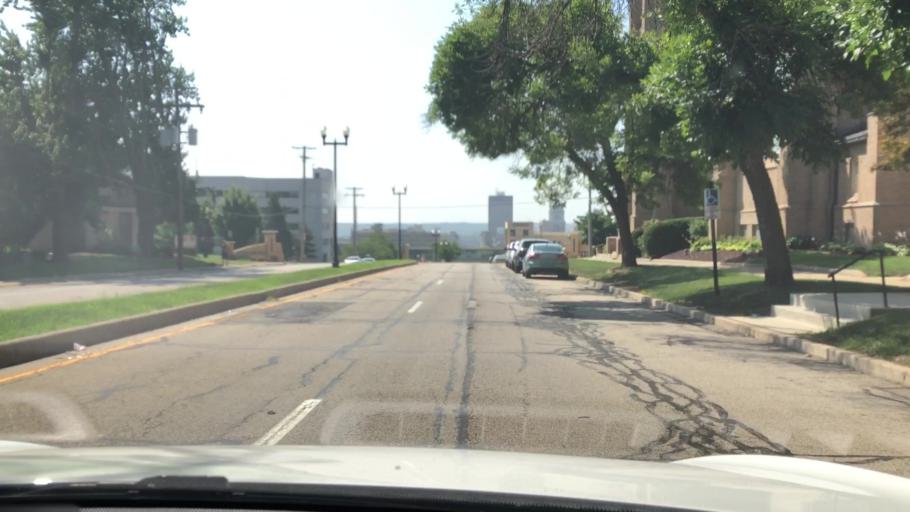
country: US
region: Illinois
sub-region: Peoria County
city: Peoria
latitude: 40.7017
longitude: -89.5979
